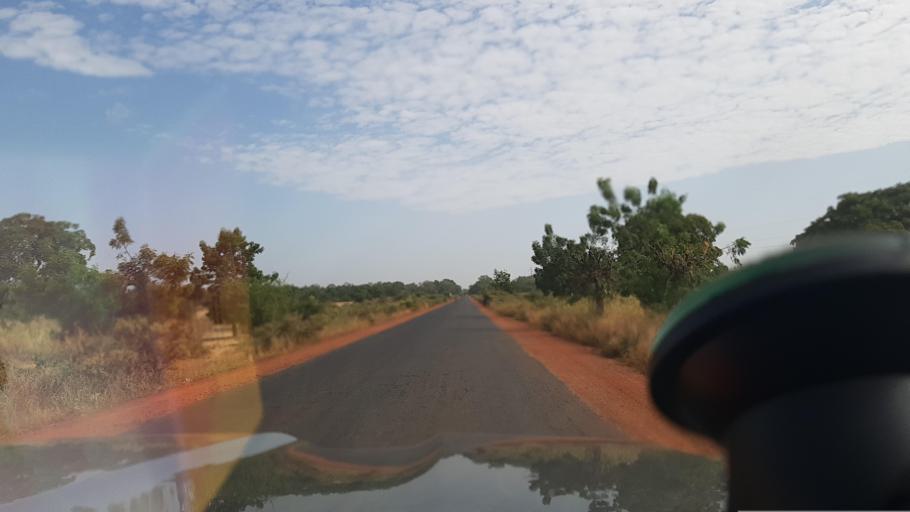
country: ML
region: Segou
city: Segou
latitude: 13.5229
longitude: -6.1332
